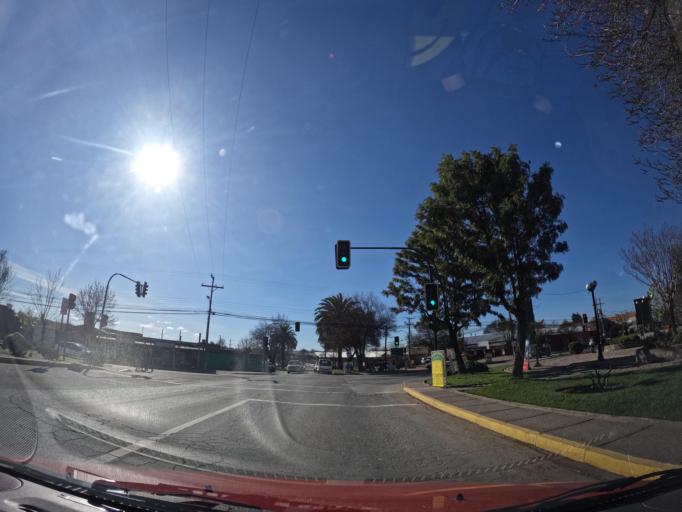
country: CL
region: Maule
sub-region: Provincia de Cauquenes
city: Cauquenes
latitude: -35.9813
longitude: -72.3159
